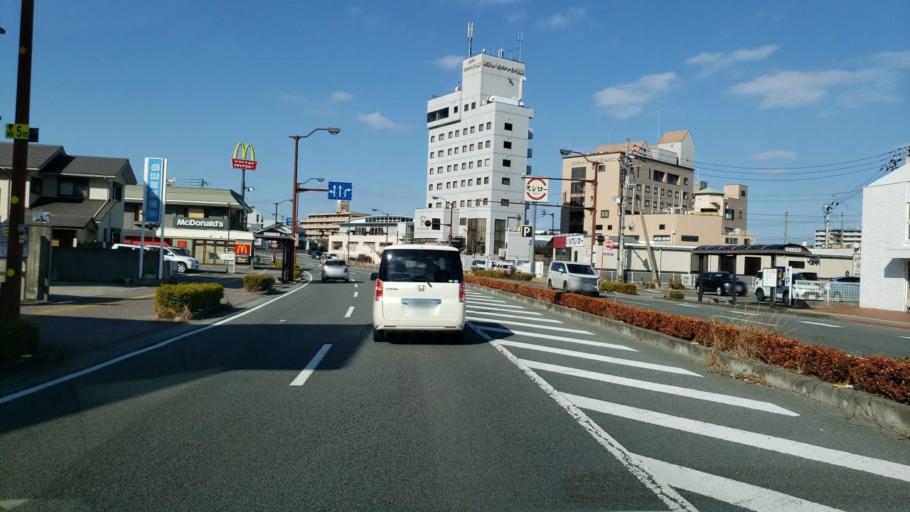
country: JP
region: Tokushima
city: Tokushima-shi
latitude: 34.0764
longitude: 134.5455
